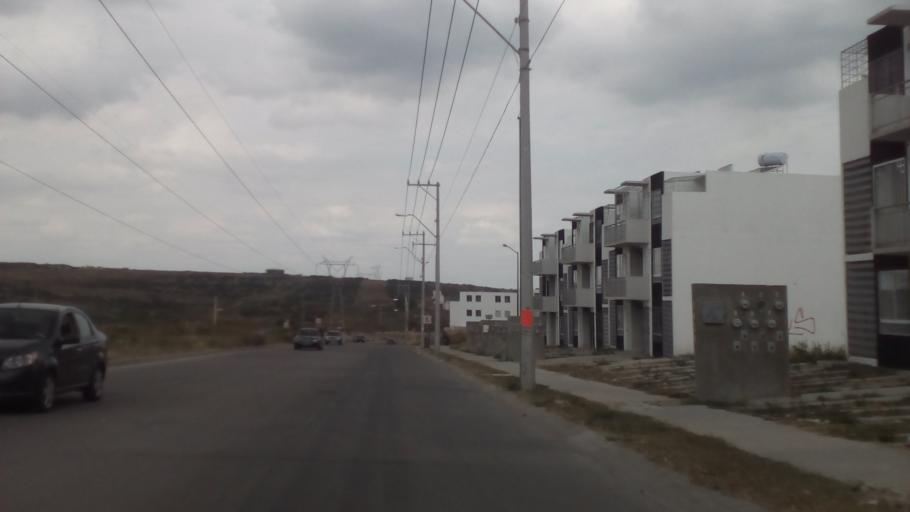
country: MX
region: Guanajuato
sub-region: Leon
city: Fraccionamiento Paseo de las Torres
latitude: 21.1766
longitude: -101.7654
